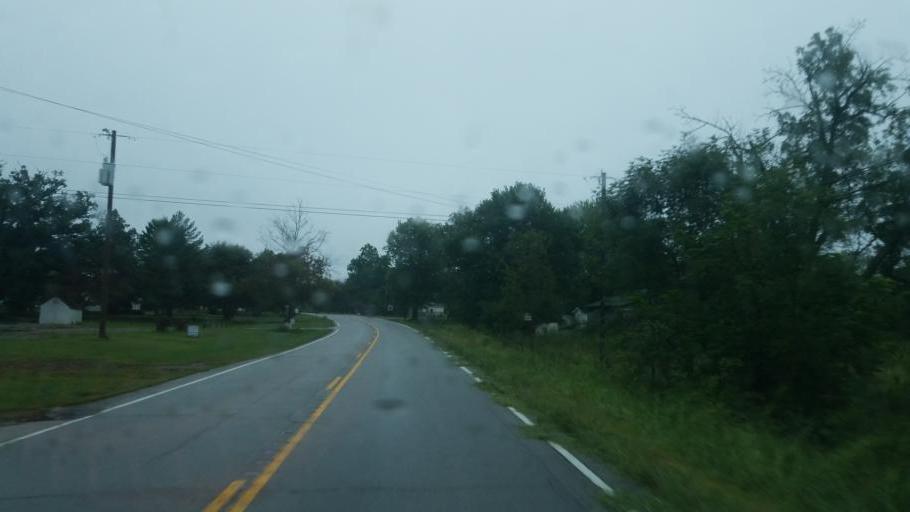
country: US
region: Kentucky
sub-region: Fleming County
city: Flemingsburg
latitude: 38.3844
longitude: -83.6562
